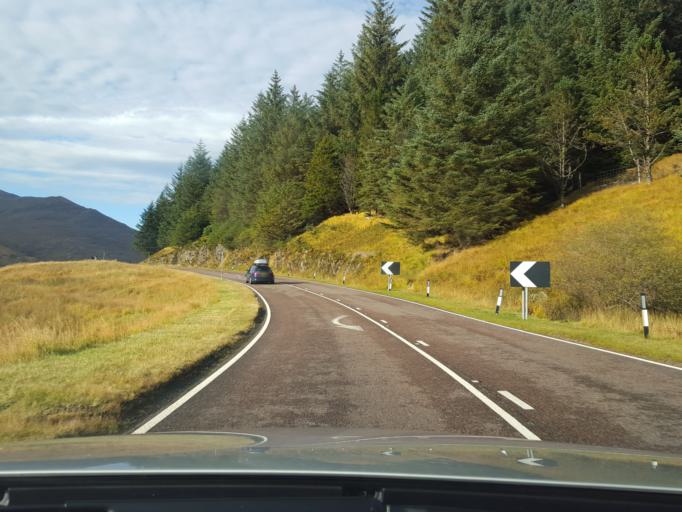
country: GB
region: Scotland
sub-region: Highland
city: Fort William
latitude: 57.1526
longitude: -5.2360
